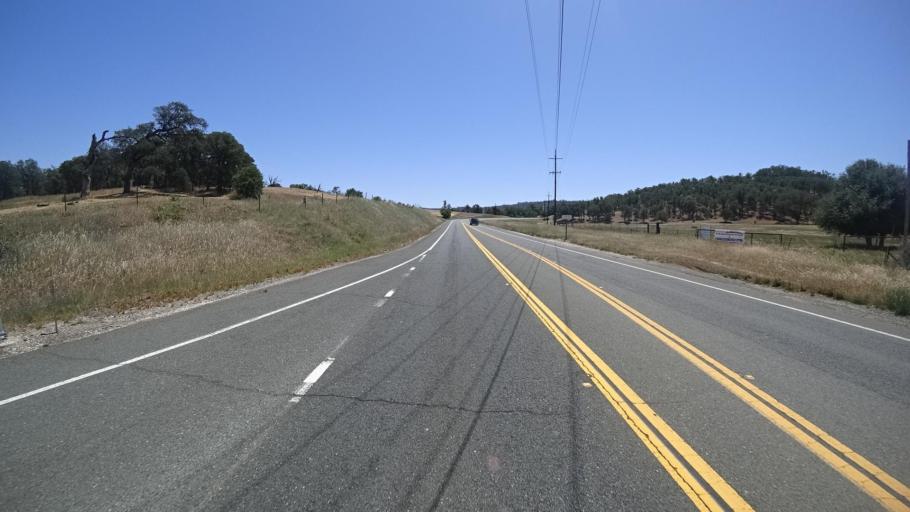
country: US
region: California
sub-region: Lake County
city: Lower Lake
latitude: 38.8888
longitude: -122.6042
